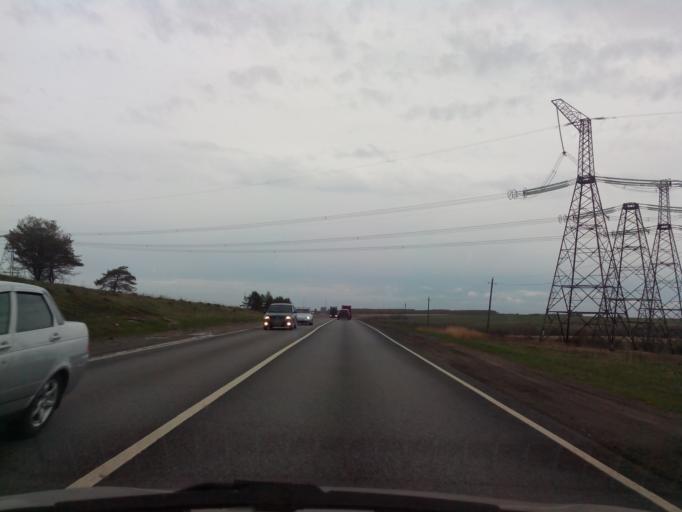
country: RU
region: Moskovskaya
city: Ozherel'ye
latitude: 54.7273
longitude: 38.2682
